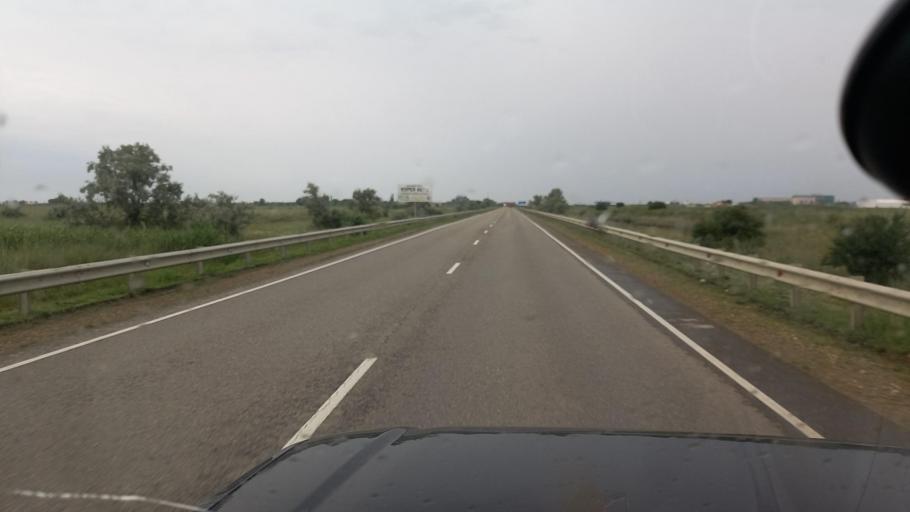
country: RU
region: Krasnodarskiy
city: Temryuk
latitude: 45.2891
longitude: 37.3435
